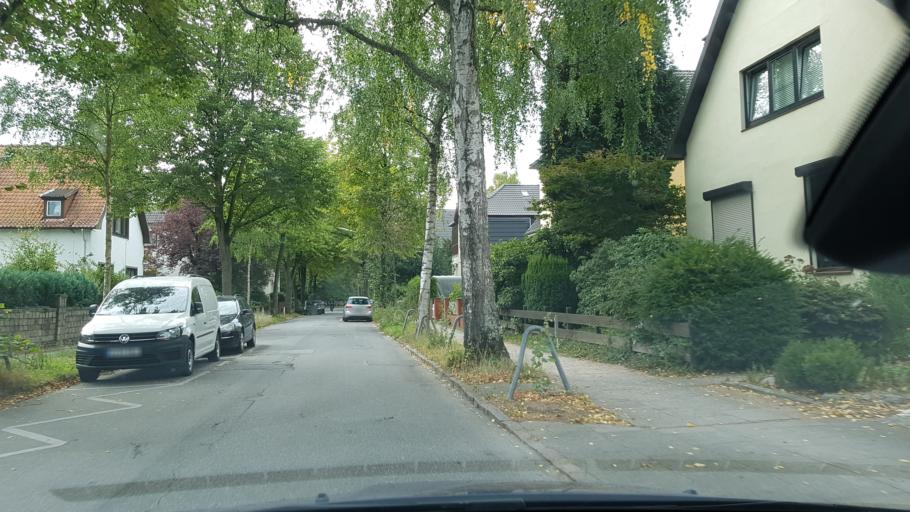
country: DE
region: Hamburg
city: Steilshoop
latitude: 53.6013
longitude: 10.0594
